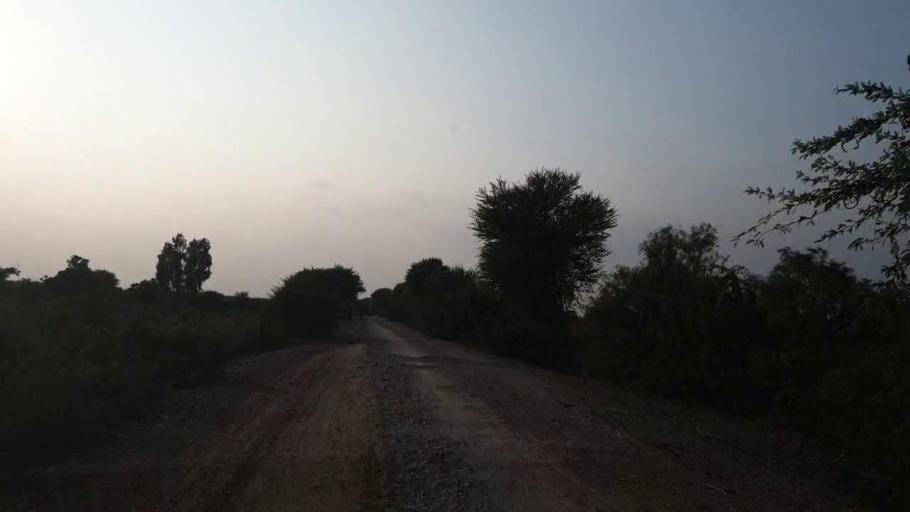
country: PK
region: Sindh
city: Tando Ghulam Ali
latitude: 25.0526
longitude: 68.9627
